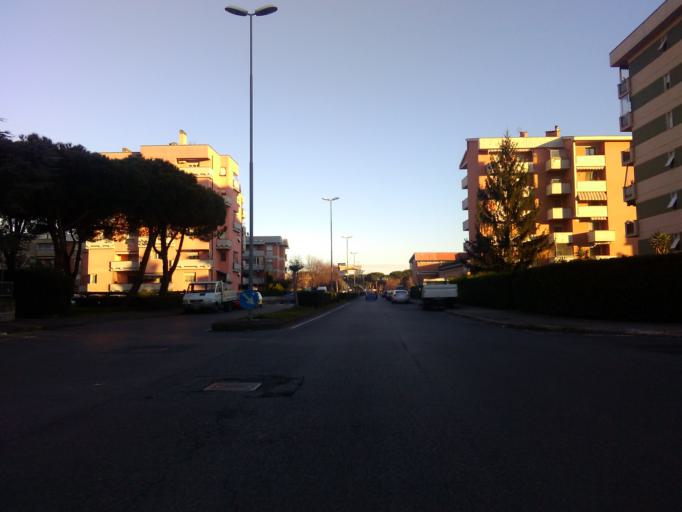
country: IT
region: Tuscany
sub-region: Provincia di Massa-Carrara
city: Carrara
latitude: 44.0547
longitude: 10.0465
